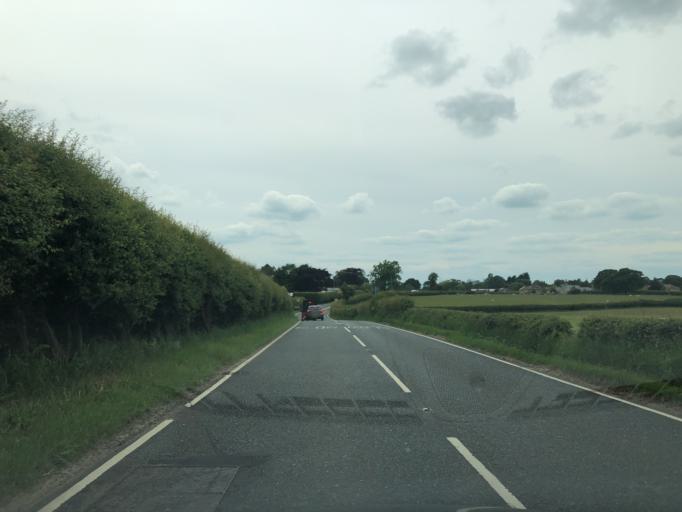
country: GB
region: England
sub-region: North Yorkshire
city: Angram Grange
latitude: 54.2347
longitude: -1.2470
